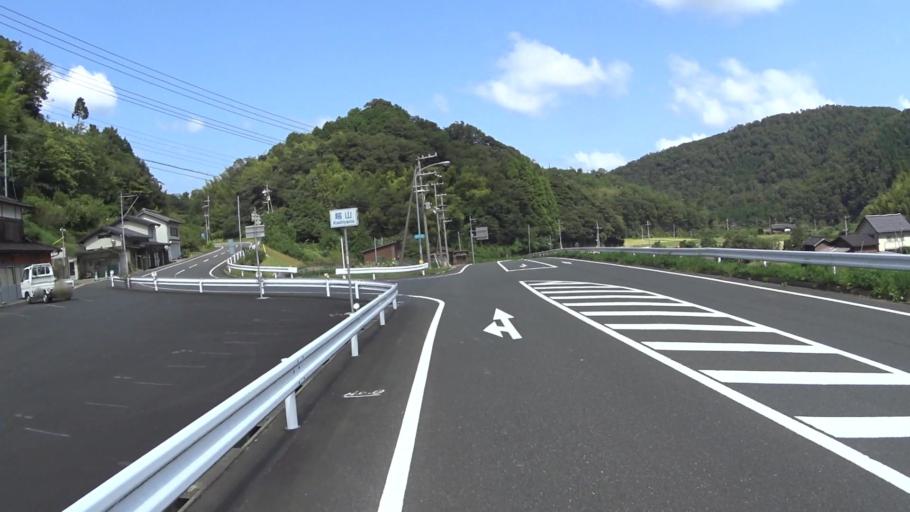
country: JP
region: Kyoto
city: Miyazu
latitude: 35.7034
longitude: 135.2503
